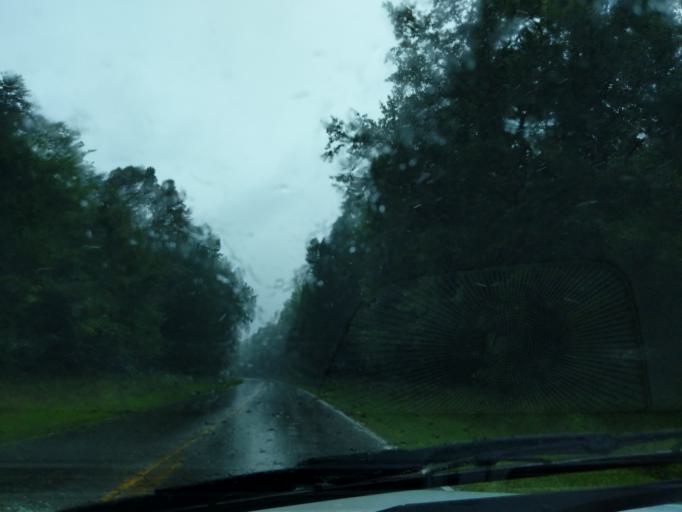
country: US
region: Kentucky
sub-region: Barren County
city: Cave City
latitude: 37.1432
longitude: -86.0870
